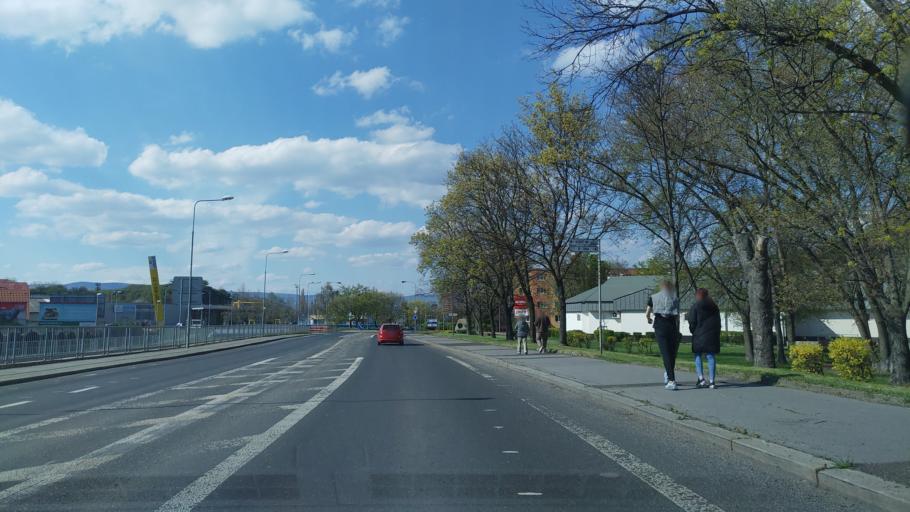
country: CZ
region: Ustecky
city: Bilina
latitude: 50.5495
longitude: 13.7736
